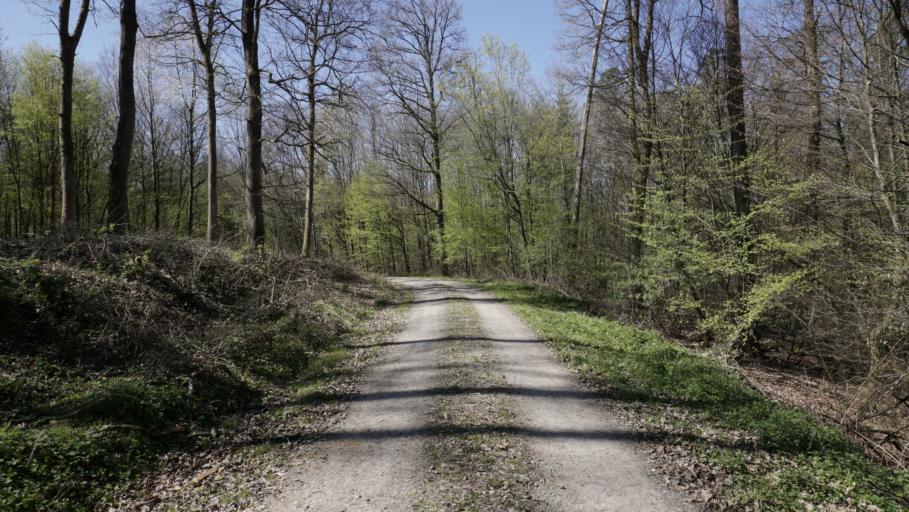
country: DE
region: Baden-Wuerttemberg
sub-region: Karlsruhe Region
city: Fahrenbach
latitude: 49.4127
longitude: 9.1770
